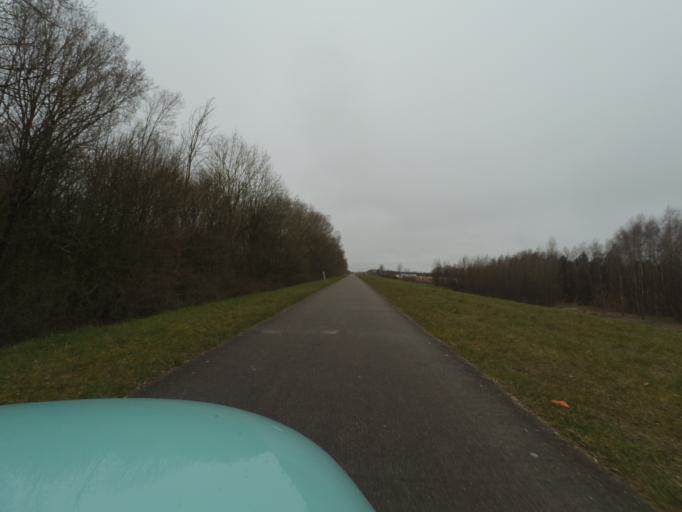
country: NL
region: Flevoland
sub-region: Gemeente Zeewolde
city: Zeewolde
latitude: 52.3151
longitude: 5.5475
